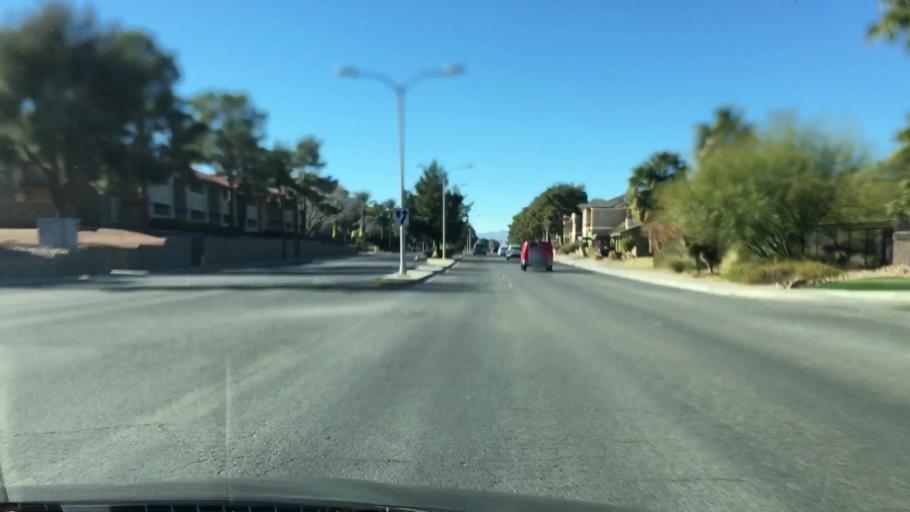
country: US
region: Nevada
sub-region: Clark County
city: Whitney
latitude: 36.0565
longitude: -115.0803
